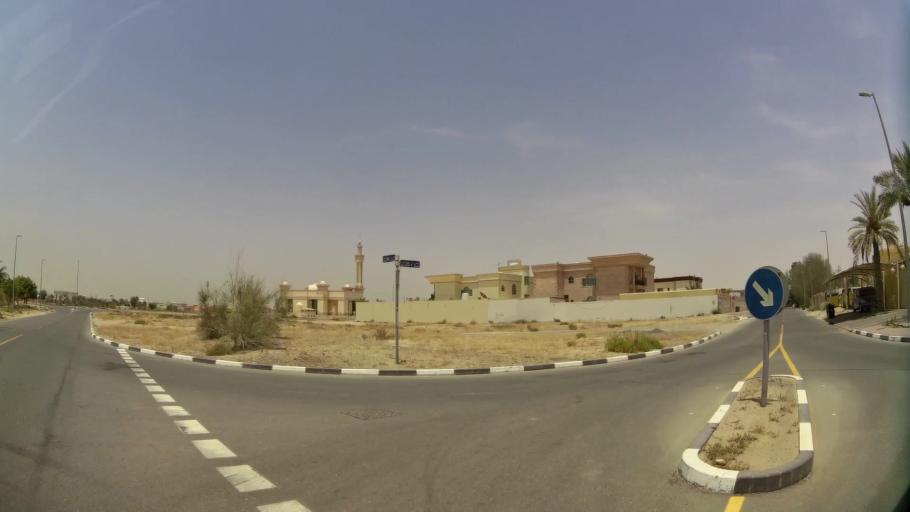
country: AE
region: Ash Shariqah
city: Sharjah
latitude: 25.2475
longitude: 55.4612
